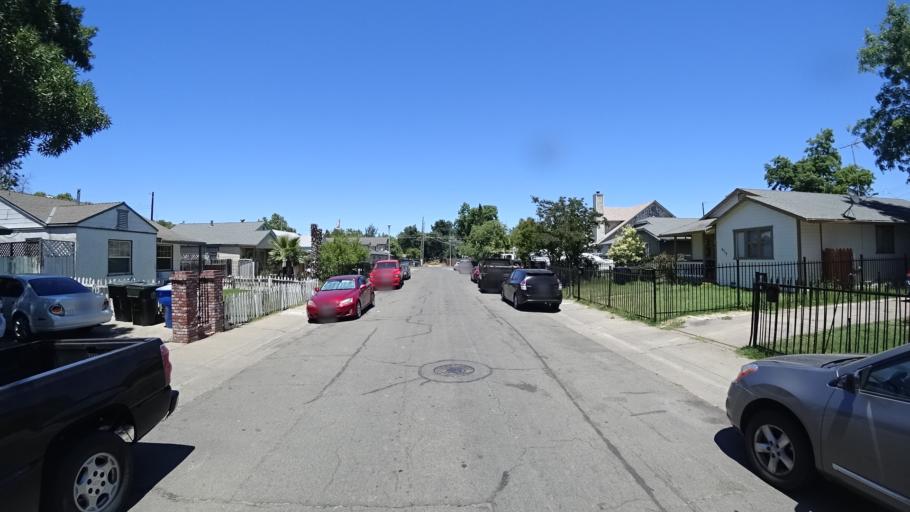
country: US
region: California
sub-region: Sacramento County
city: Parkway
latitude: 38.5369
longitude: -121.4717
